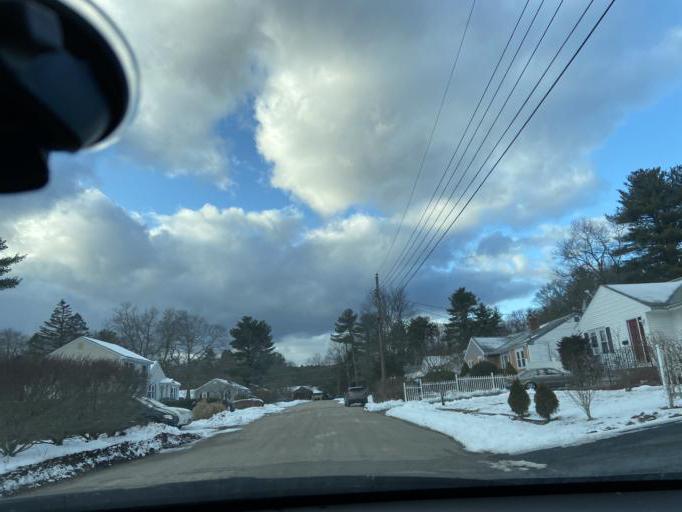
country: US
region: Massachusetts
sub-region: Norfolk County
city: Sharon
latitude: 42.1101
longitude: -71.2010
